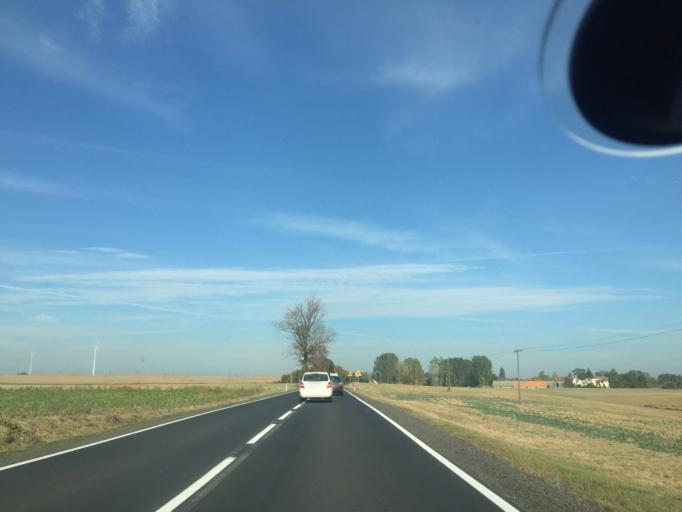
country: PL
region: Greater Poland Voivodeship
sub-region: Powiat gnieznienski
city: Trzemeszno
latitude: 52.5811
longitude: 17.8685
